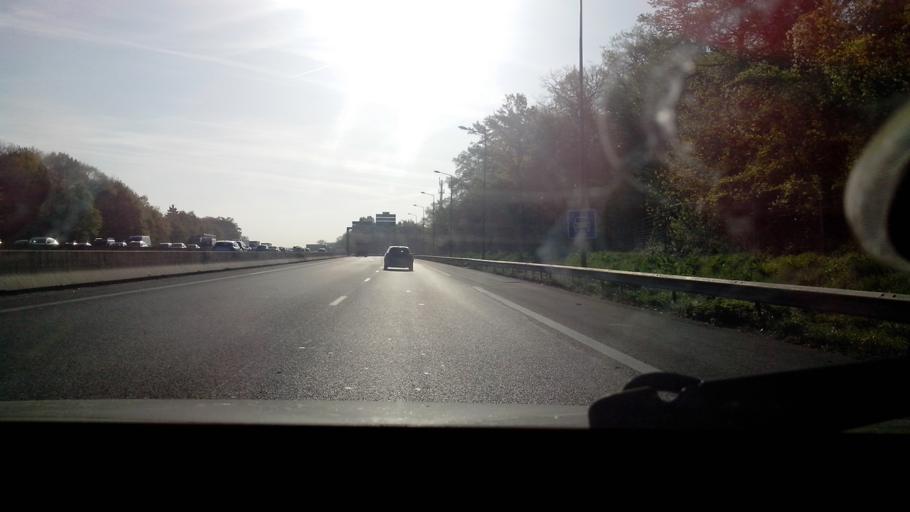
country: FR
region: Ile-de-France
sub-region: Departement de Seine-et-Marne
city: Lognes
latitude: 48.8303
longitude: 2.6098
